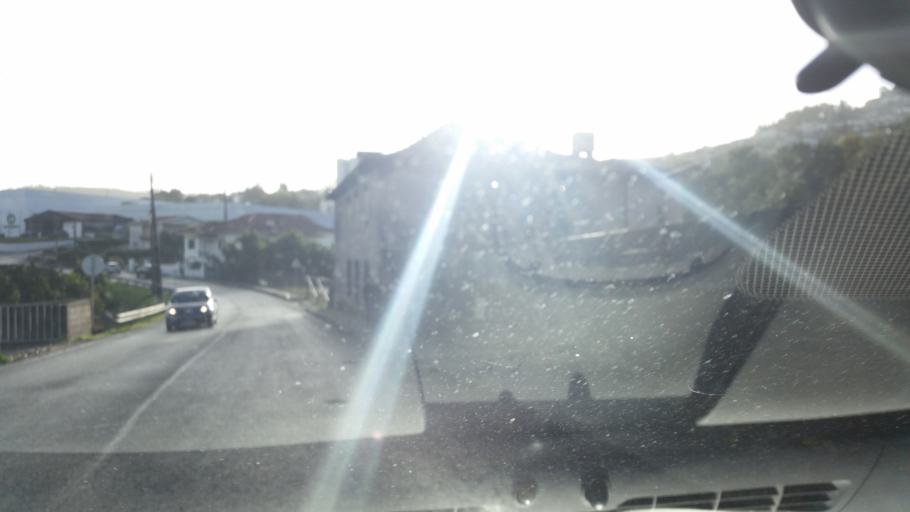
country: PT
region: Porto
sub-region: Santo Tirso
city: Aves
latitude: 41.3549
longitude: -8.4216
